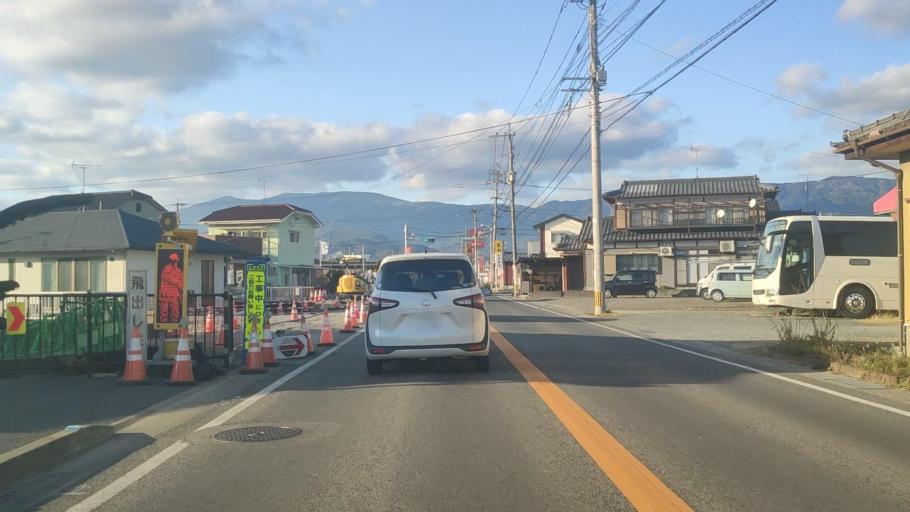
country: JP
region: Saga Prefecture
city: Saga-shi
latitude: 33.2745
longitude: 130.2174
